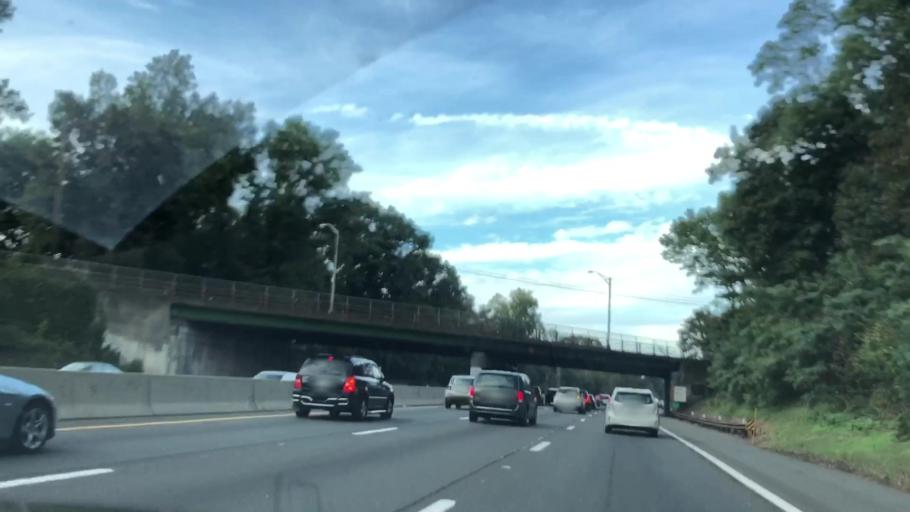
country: US
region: New Jersey
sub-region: Essex County
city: Bloomfield
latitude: 40.8159
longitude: -74.1794
